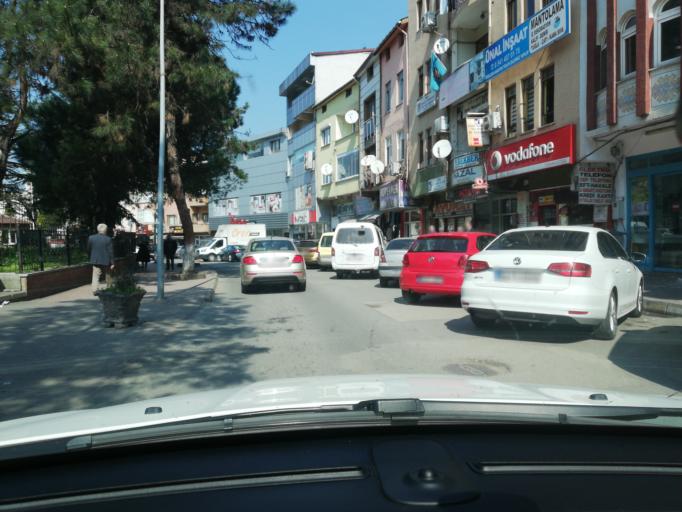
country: TR
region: Karabuk
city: Yenice
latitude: 41.2007
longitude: 32.3289
